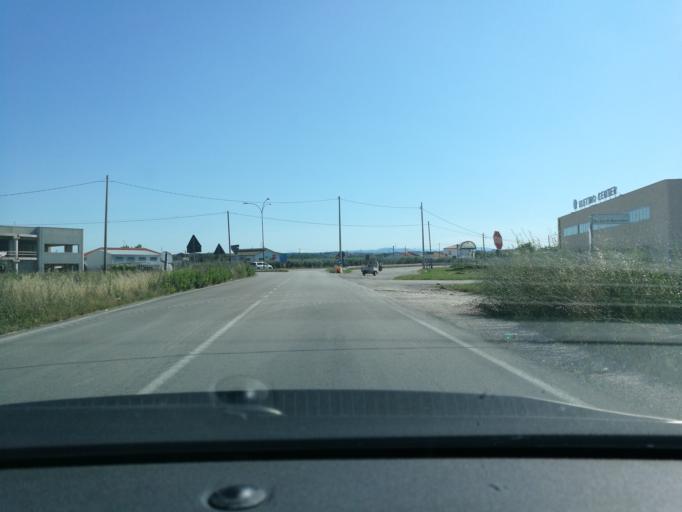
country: IT
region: Abruzzo
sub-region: Provincia di Chieti
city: Vasto
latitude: 42.1685
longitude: 14.6948
